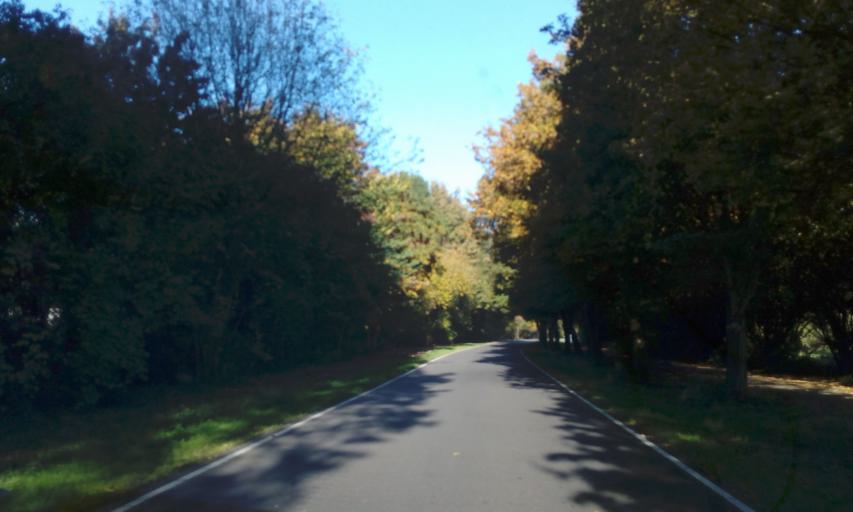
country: NL
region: South Holland
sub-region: Gemeente Lansingerland
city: Bleiswijk
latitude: 52.0092
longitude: 4.5481
